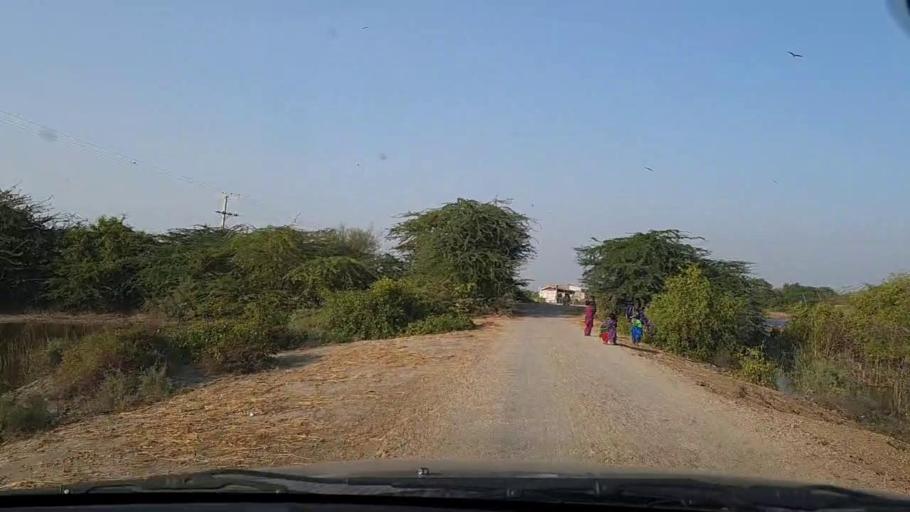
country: PK
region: Sindh
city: Chuhar Jamali
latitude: 24.2985
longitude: 67.7553
